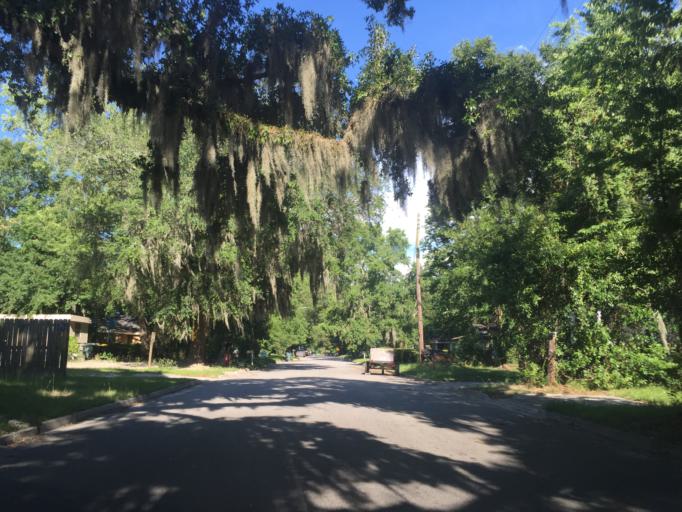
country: US
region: Georgia
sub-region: Chatham County
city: Montgomery
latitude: 31.9966
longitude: -81.1213
